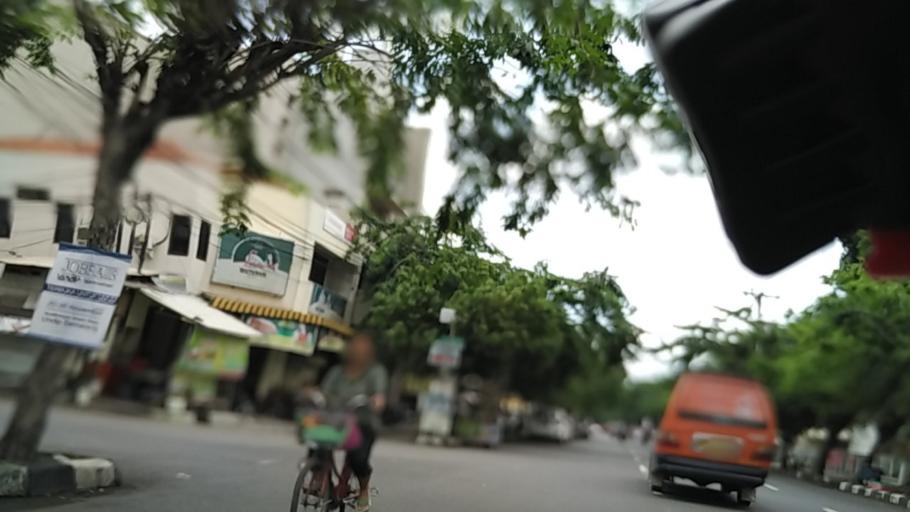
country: ID
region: Central Java
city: Semarang
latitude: -6.9911
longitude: 110.4319
